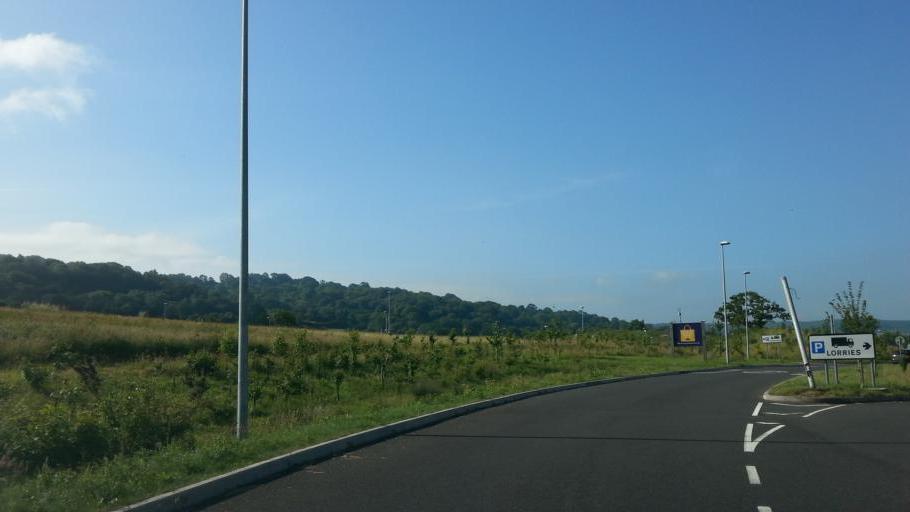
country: GB
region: England
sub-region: Gloucestershire
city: Painswick
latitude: 51.8202
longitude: -2.2232
